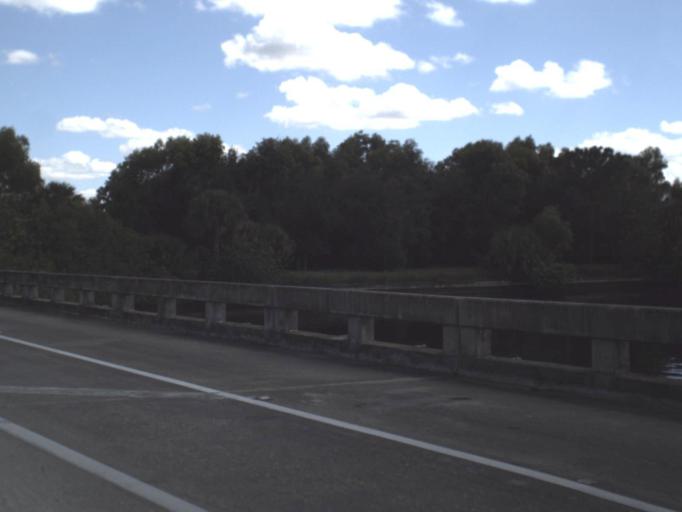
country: US
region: Florida
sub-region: Collier County
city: Marco
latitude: 25.9594
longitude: -81.5100
